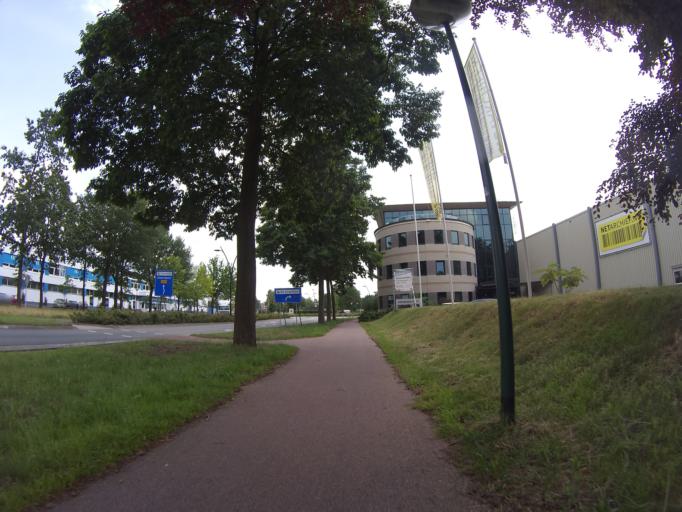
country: NL
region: Utrecht
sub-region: Gemeente Soest
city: Soest
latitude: 52.1802
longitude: 5.2680
